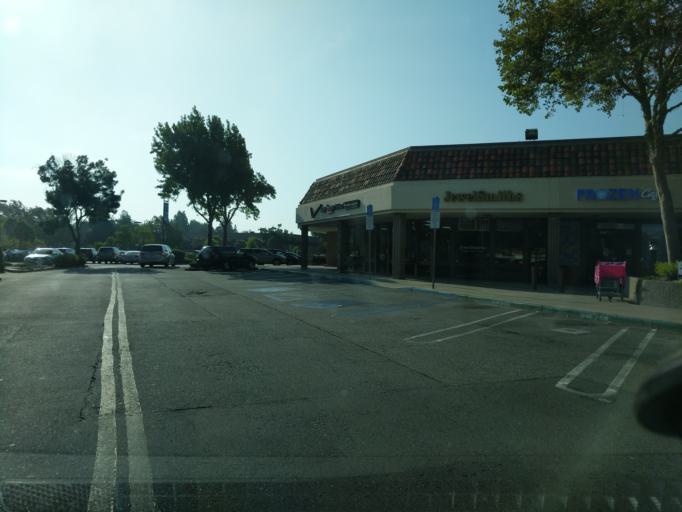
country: US
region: California
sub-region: Contra Costa County
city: San Ramon
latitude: 37.7740
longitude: -121.9772
